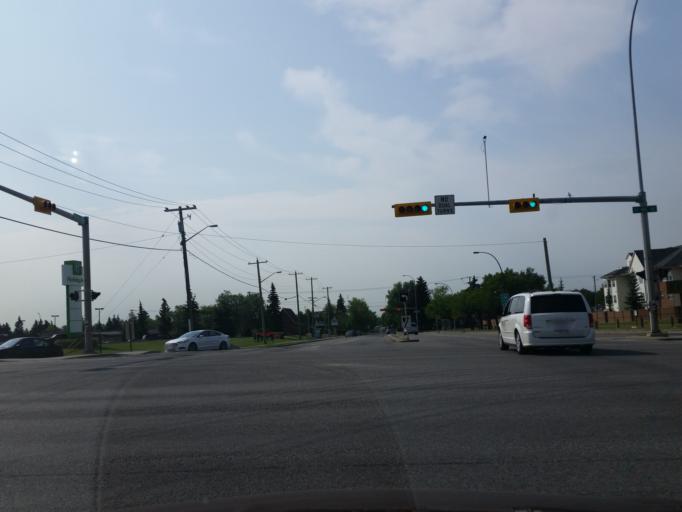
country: CA
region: Alberta
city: Calgary
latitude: 51.0671
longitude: -114.0134
